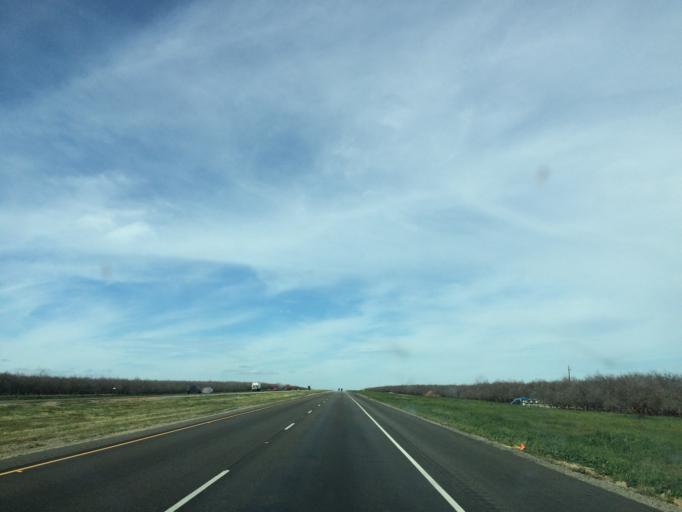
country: US
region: California
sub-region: Merced County
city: South Dos Palos
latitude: 36.7412
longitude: -120.6985
